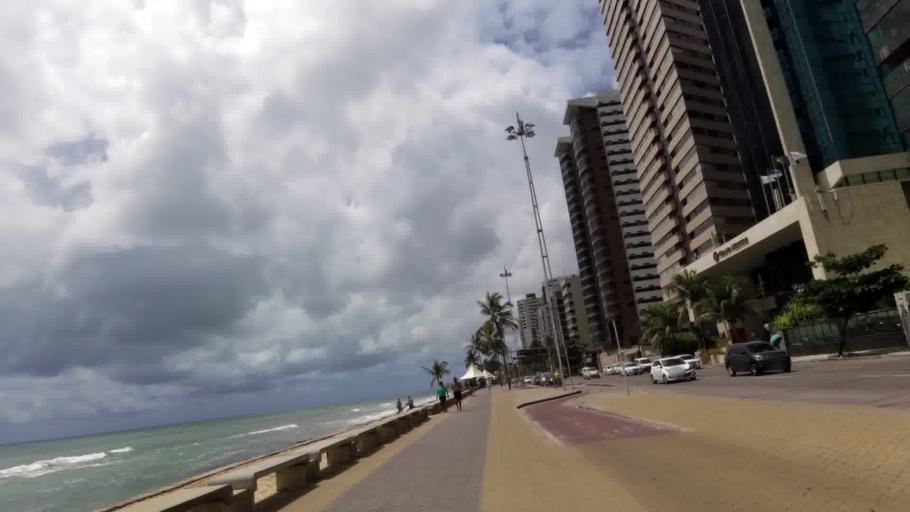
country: BR
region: Pernambuco
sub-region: Recife
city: Recife
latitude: -8.1360
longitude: -34.9015
